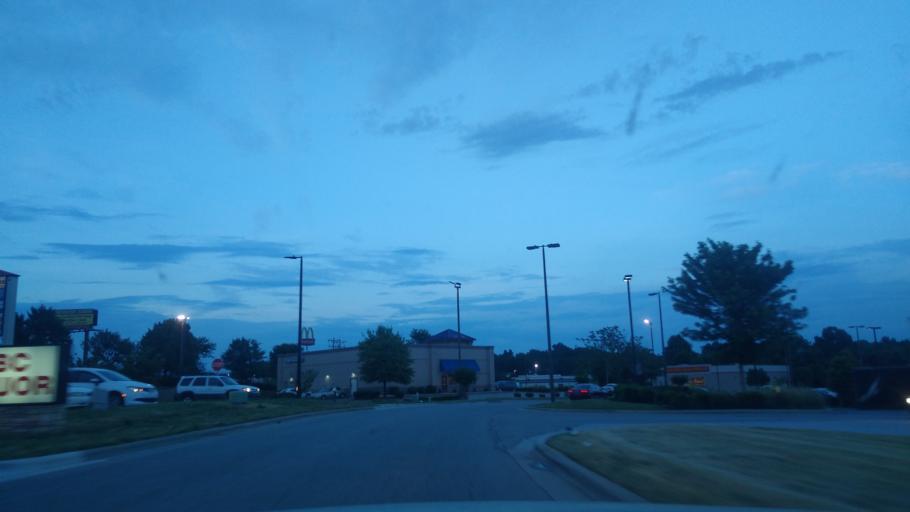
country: US
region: North Carolina
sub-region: Guilford County
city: Greensboro
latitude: 36.1117
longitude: -79.7555
